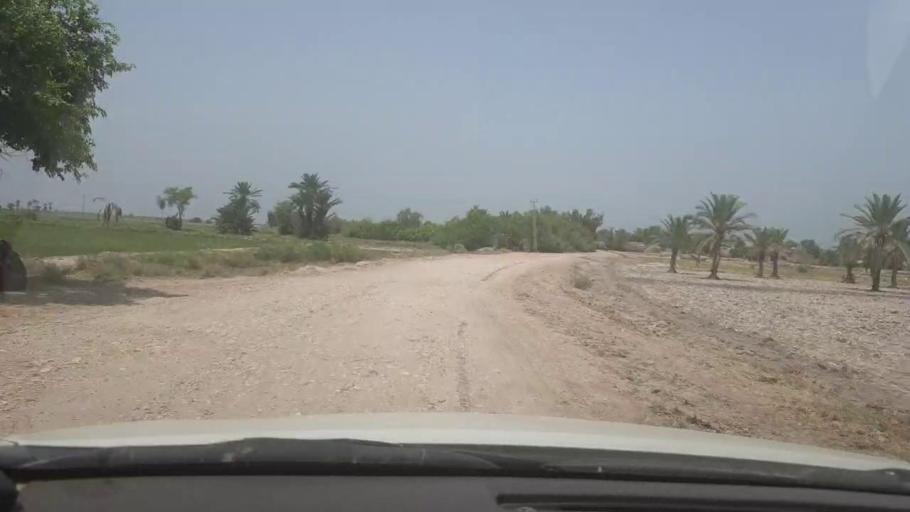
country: PK
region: Sindh
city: Shikarpur
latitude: 27.9459
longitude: 68.5716
